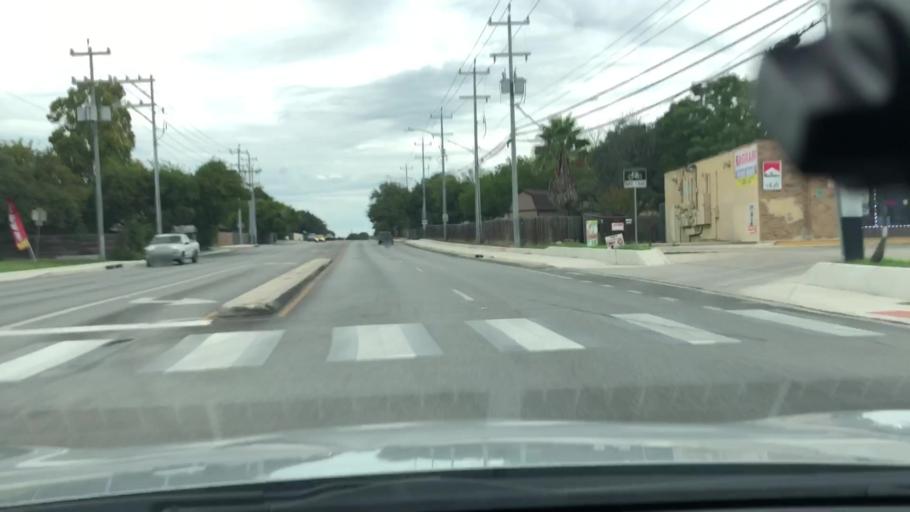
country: US
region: Texas
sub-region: Bexar County
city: Leon Valley
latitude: 29.4903
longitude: -98.6654
